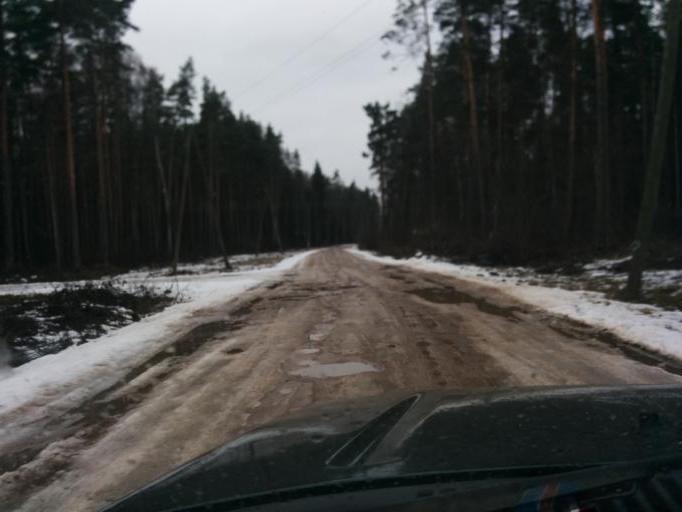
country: LV
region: Ozolnieku
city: Ozolnieki
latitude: 56.6806
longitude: 23.7608
